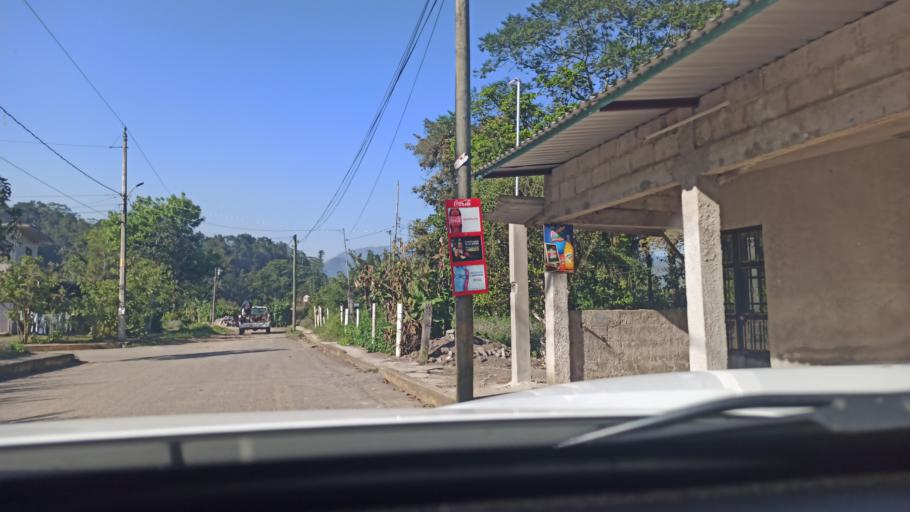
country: MX
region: Veracruz
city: Atzacan
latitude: 18.9116
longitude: -97.0923
